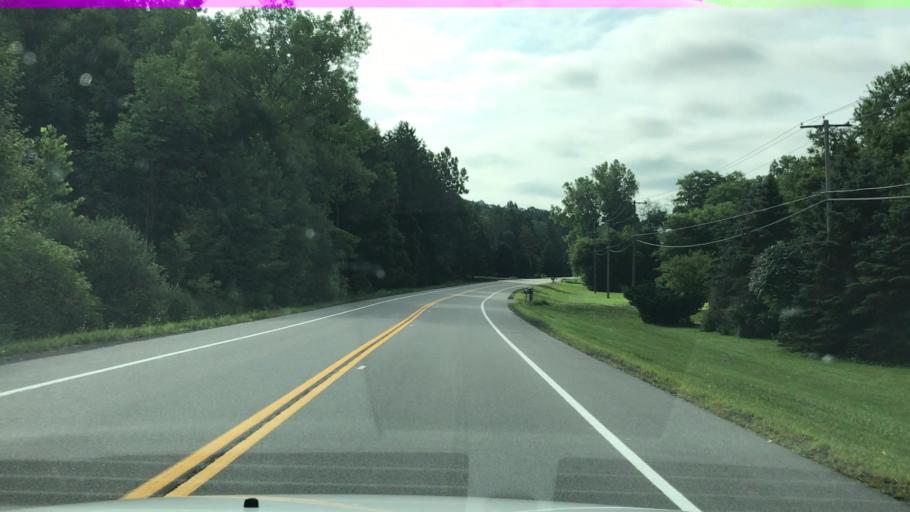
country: US
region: New York
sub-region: Erie County
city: Alden
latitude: 42.8555
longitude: -78.4961
